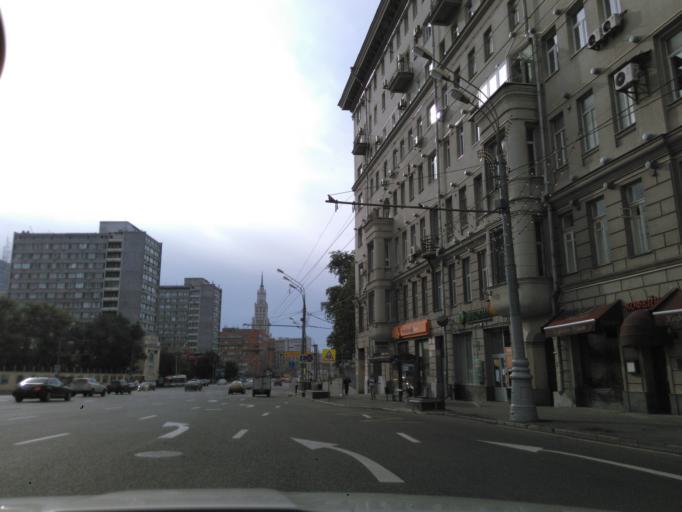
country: RU
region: Moscow
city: Moscow
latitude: 55.7718
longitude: 37.6378
